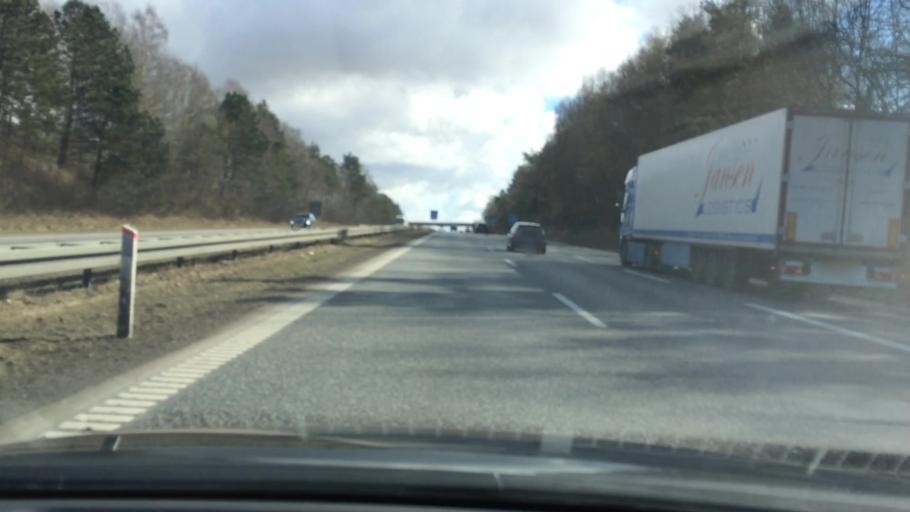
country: DK
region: Central Jutland
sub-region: Randers Kommune
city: Randers
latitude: 56.4408
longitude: 10.0146
